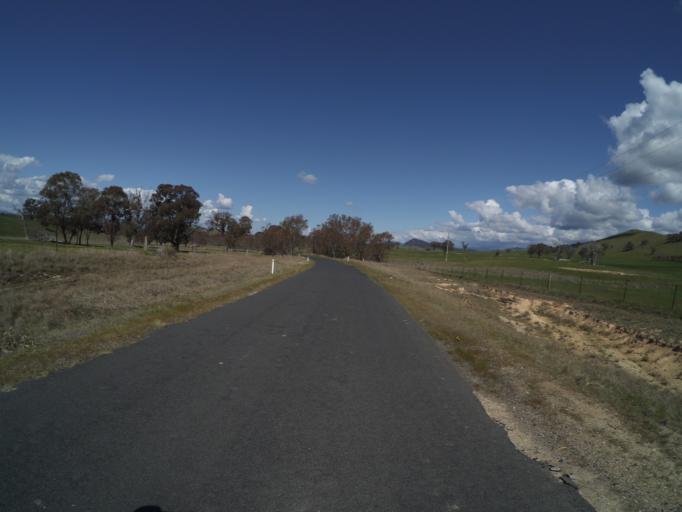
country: AU
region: New South Wales
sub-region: Yass Valley
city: Murrumbateman
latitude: -35.0978
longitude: 148.8541
